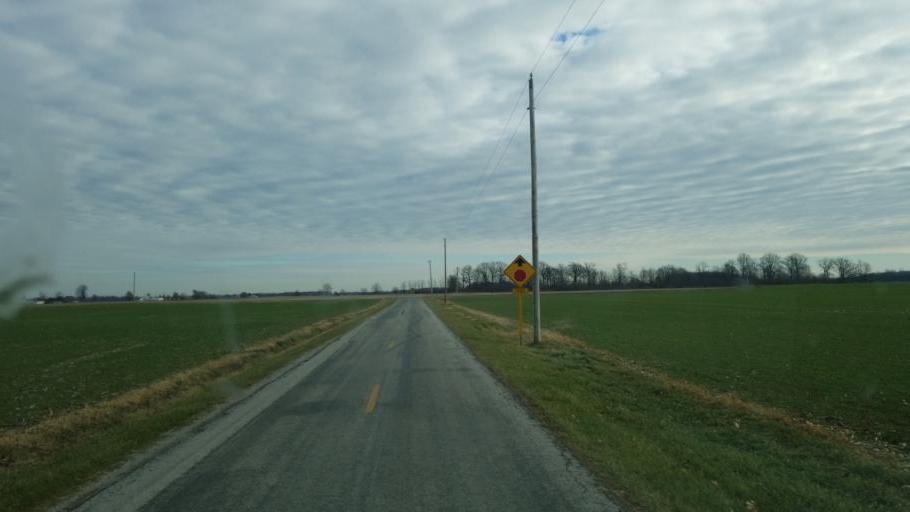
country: US
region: Ohio
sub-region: Union County
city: Richwood
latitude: 40.5270
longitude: -83.3161
